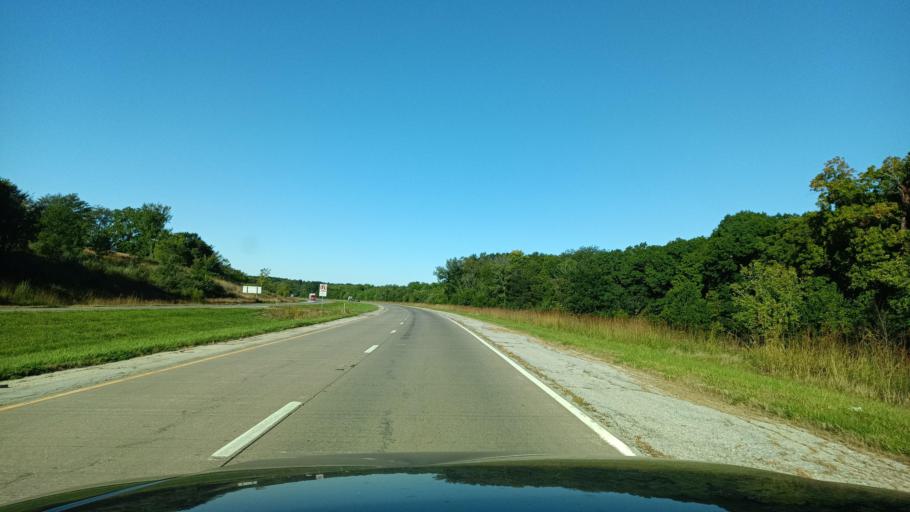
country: US
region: Illinois
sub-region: Warren County
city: Monmouth
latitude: 40.9223
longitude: -90.5311
